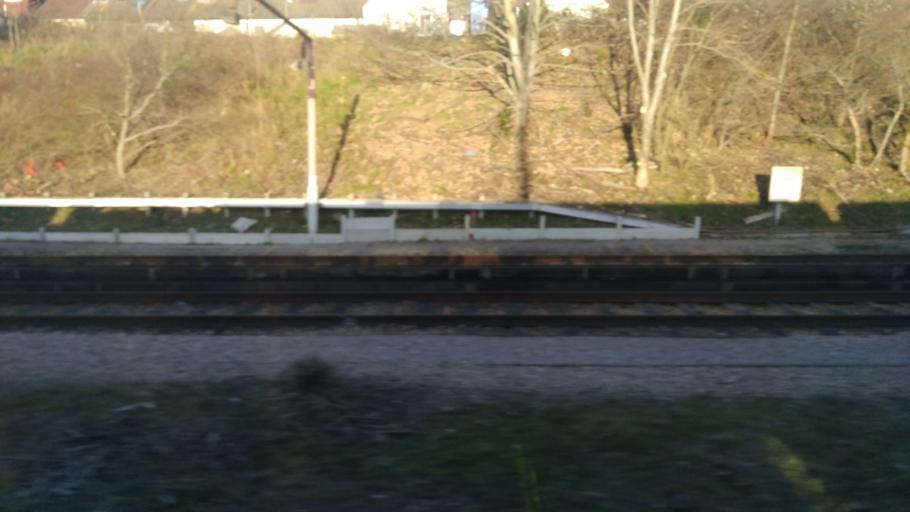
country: GB
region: England
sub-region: Kent
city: Tonbridge
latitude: 51.1924
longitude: 0.2637
